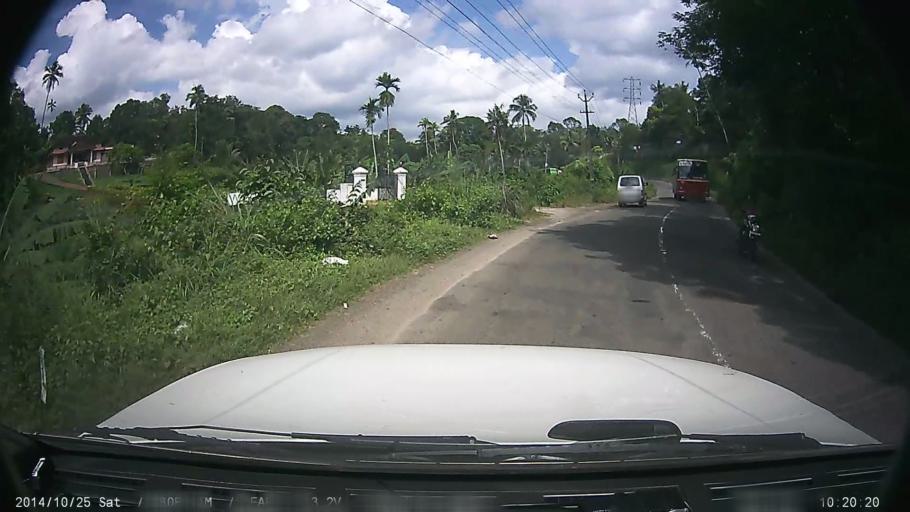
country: IN
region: Kerala
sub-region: Ernakulam
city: Muvattupuzha
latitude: 9.8946
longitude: 76.5877
